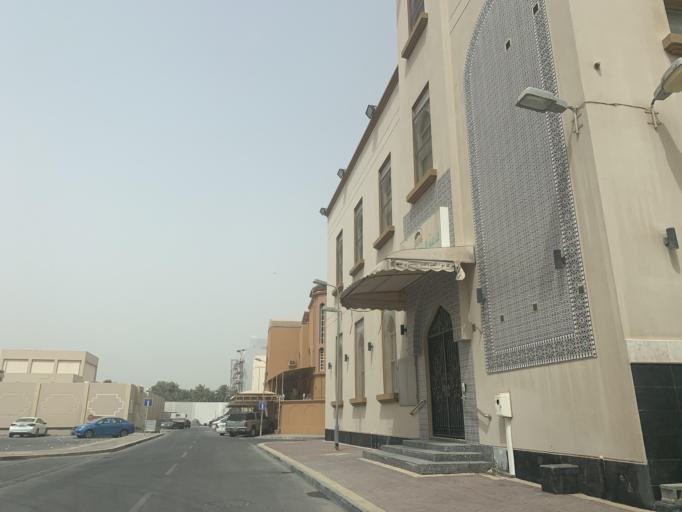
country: BH
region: Manama
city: Jidd Hafs
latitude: 26.2304
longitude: 50.5313
